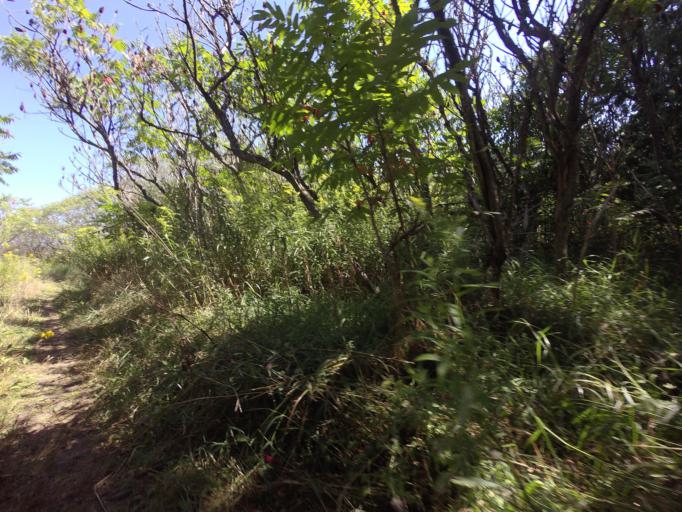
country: CA
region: Ontario
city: Orangeville
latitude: 43.8209
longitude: -80.0178
